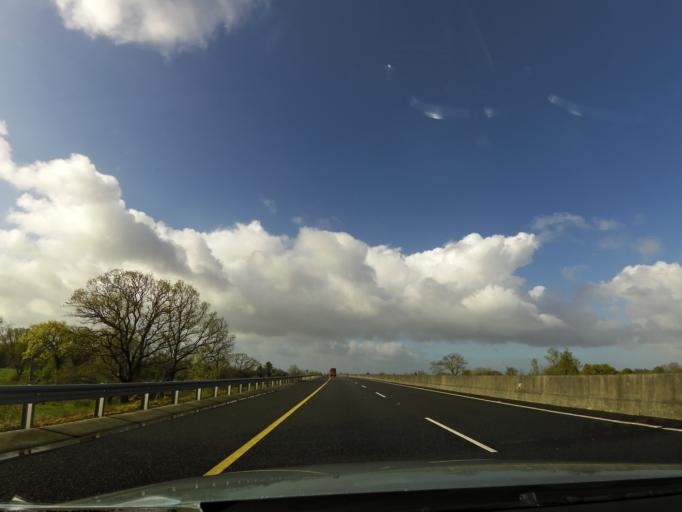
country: IE
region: Munster
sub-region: County Limerick
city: Castleconnell
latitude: 52.7087
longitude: -8.4812
